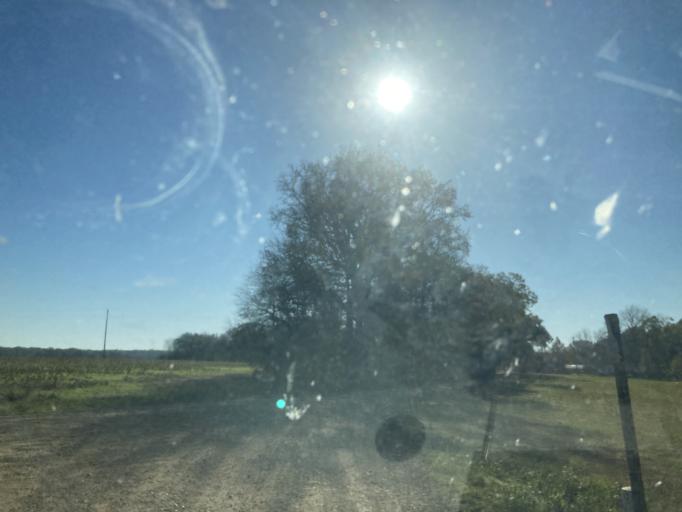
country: US
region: Mississippi
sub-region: Madison County
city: Kearney Park
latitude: 32.7258
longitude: -90.3084
